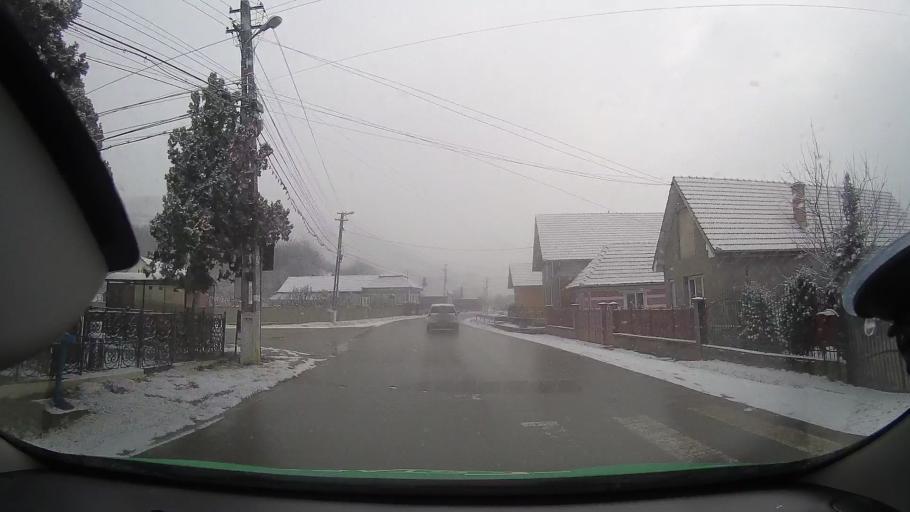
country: RO
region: Alba
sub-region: Municipiul Aiud
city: Ciumbrud
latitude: 46.3091
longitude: 23.7935
